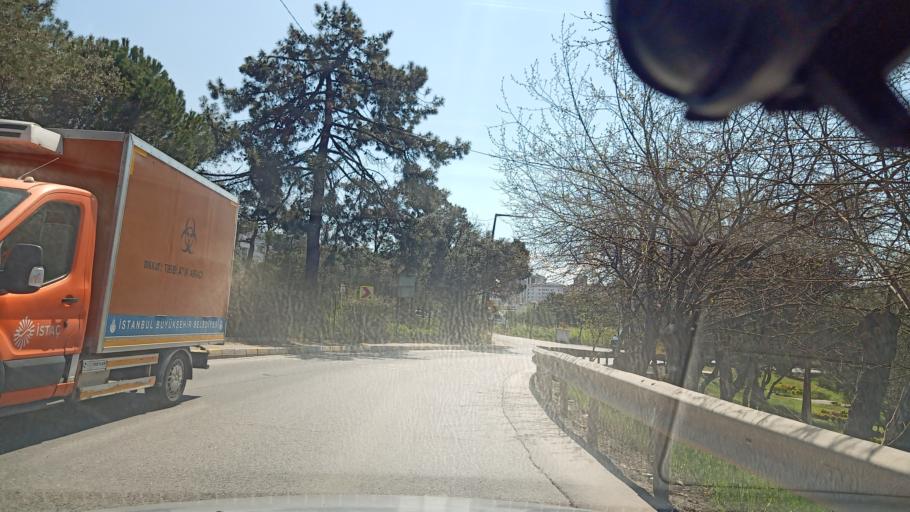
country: TR
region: Istanbul
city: Maltepe
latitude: 40.9473
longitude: 29.1447
